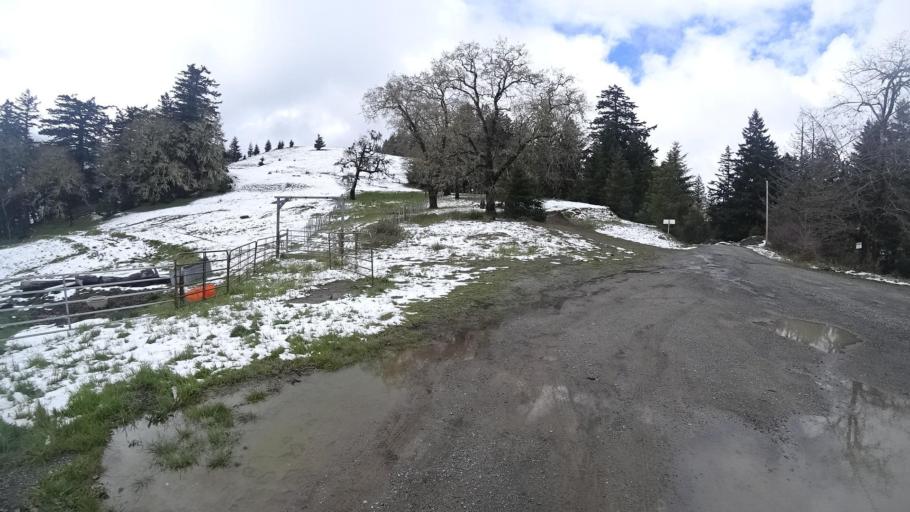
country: US
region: California
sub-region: Humboldt County
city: Blue Lake
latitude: 40.8804
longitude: -123.8709
